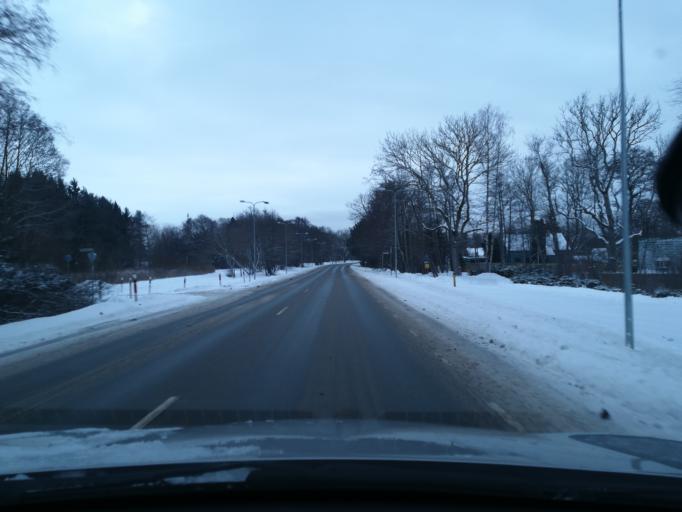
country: EE
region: Harju
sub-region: Keila linn
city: Keila
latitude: 59.4397
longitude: 24.3715
